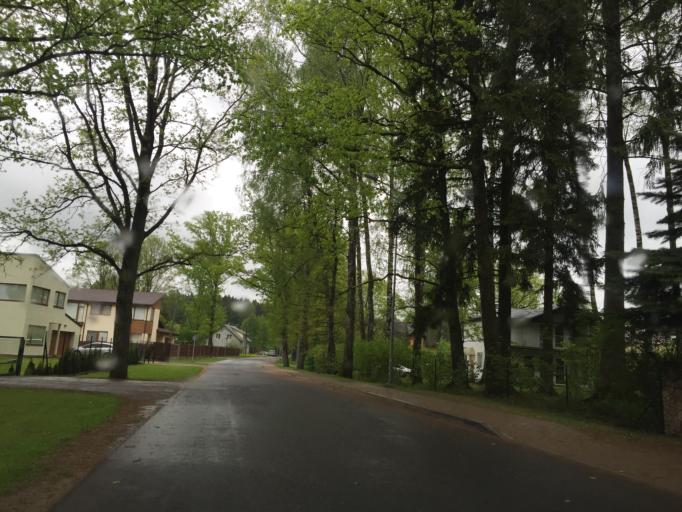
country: LV
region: Lielvarde
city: Lielvarde
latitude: 56.7261
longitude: 24.8056
